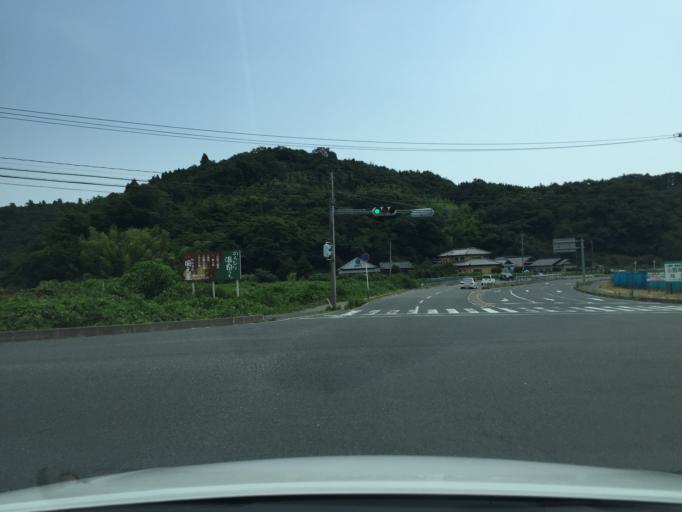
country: JP
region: Fukushima
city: Iwaki
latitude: 36.9704
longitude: 140.9172
